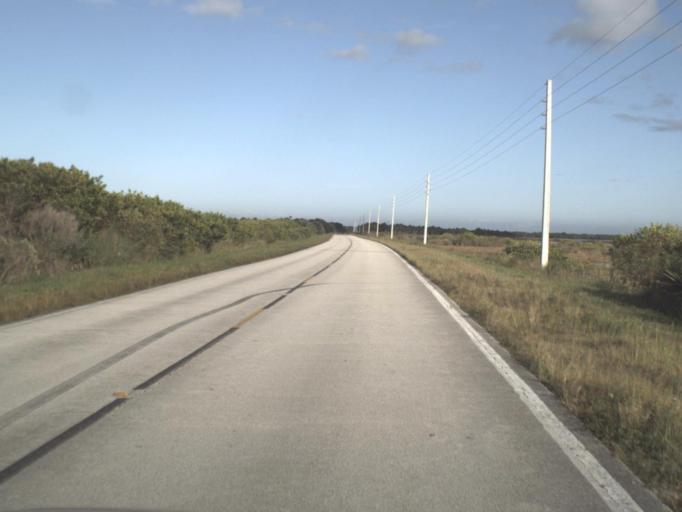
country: US
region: Florida
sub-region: Brevard County
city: Titusville
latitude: 28.6432
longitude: -80.7630
